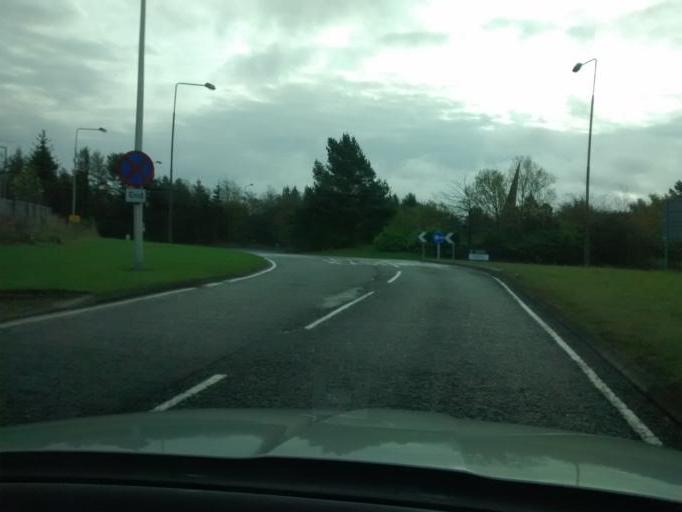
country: GB
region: Scotland
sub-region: West Lothian
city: Mid Calder
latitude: 55.8812
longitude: -3.4924
